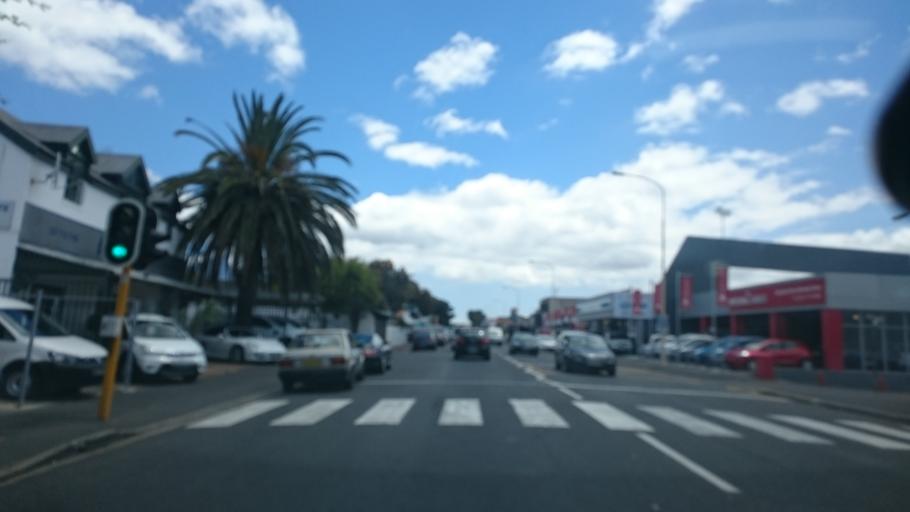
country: ZA
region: Western Cape
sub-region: City of Cape Town
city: Bergvliet
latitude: -34.0391
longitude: 18.4644
